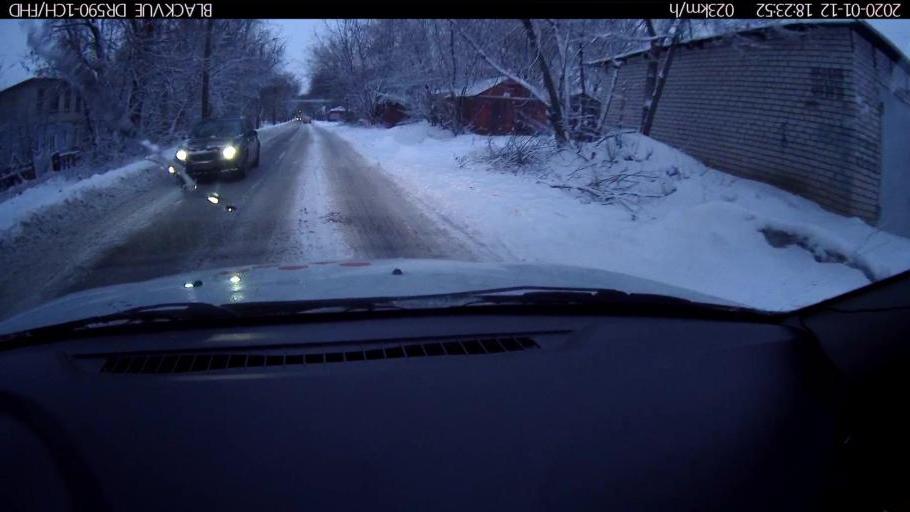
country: RU
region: Nizjnij Novgorod
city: Nizhniy Novgorod
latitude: 56.2689
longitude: 43.9352
